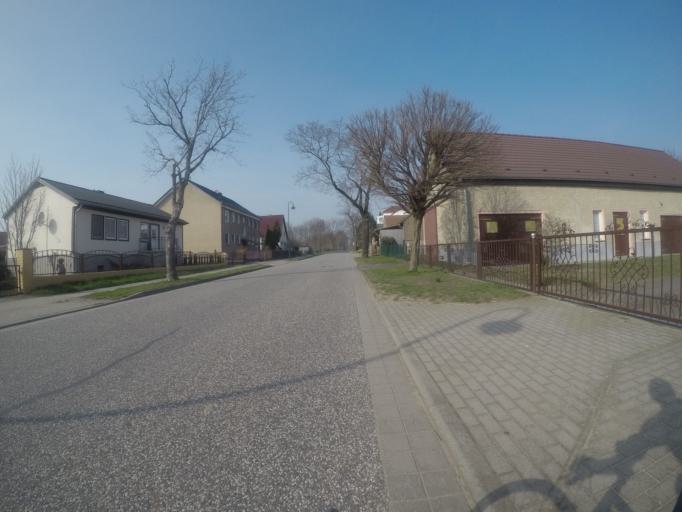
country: DE
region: Brandenburg
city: Mittenwalde
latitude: 52.3110
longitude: 13.5119
